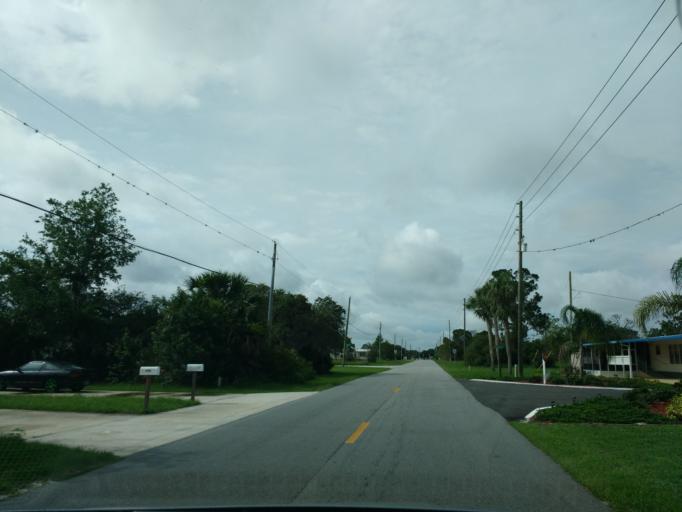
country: US
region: Florida
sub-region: Highlands County
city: Sebring
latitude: 27.4768
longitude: -81.4861
